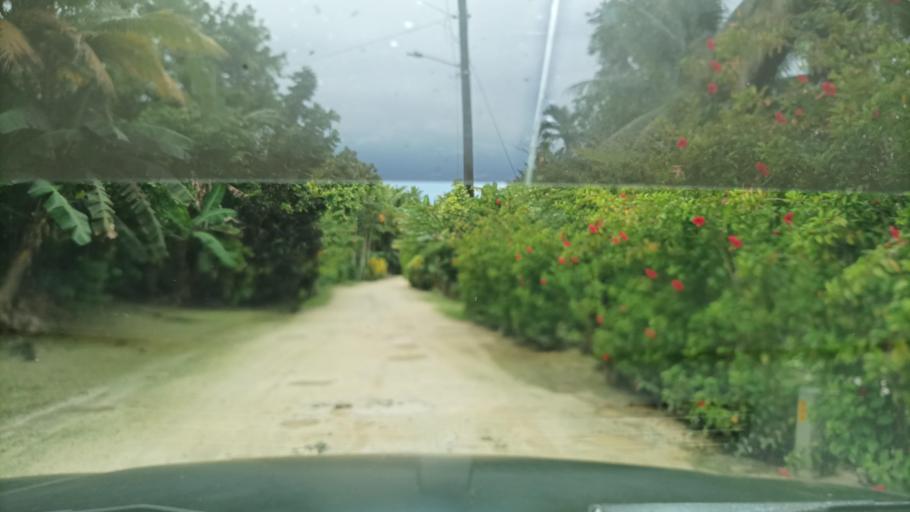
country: FM
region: Yap
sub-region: Weloy Municipality
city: Colonia
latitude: 9.5493
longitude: 138.1905
